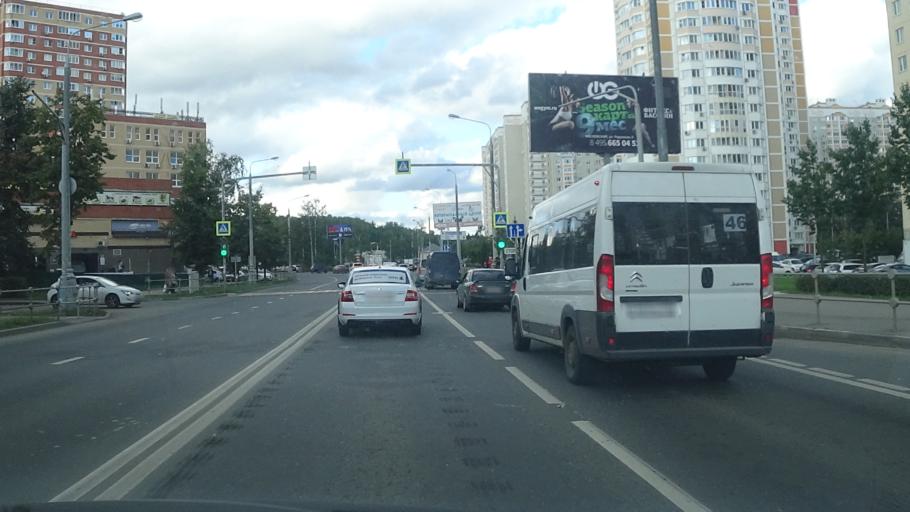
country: RU
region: Moskovskaya
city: Moskovskiy
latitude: 55.6020
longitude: 37.3565
